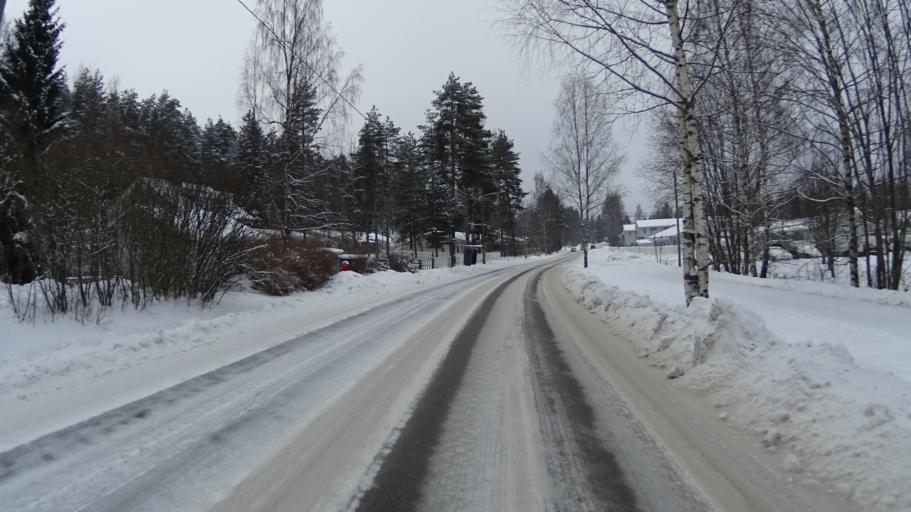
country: FI
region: Uusimaa
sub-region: Helsinki
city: Vihti
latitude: 60.3400
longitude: 24.2963
